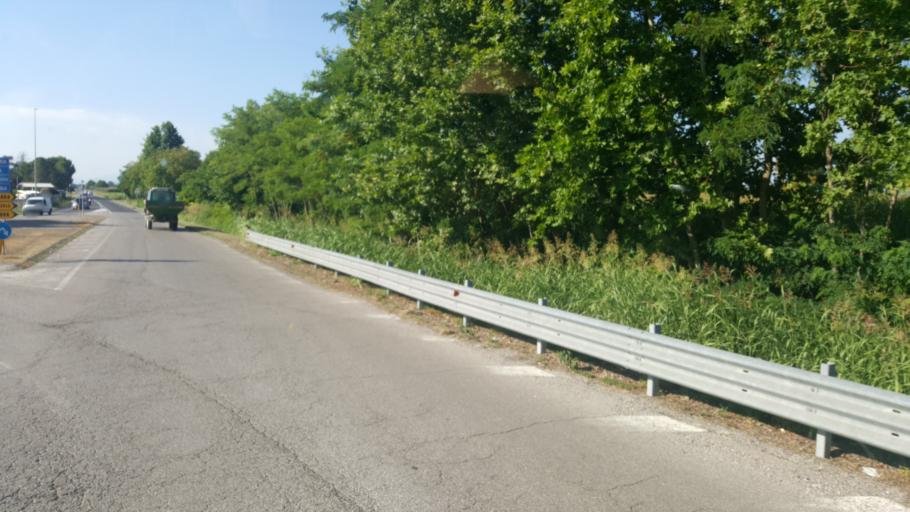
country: IT
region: Lombardy
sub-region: Provincia di Mantova
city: Medole
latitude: 45.3360
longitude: 10.5054
